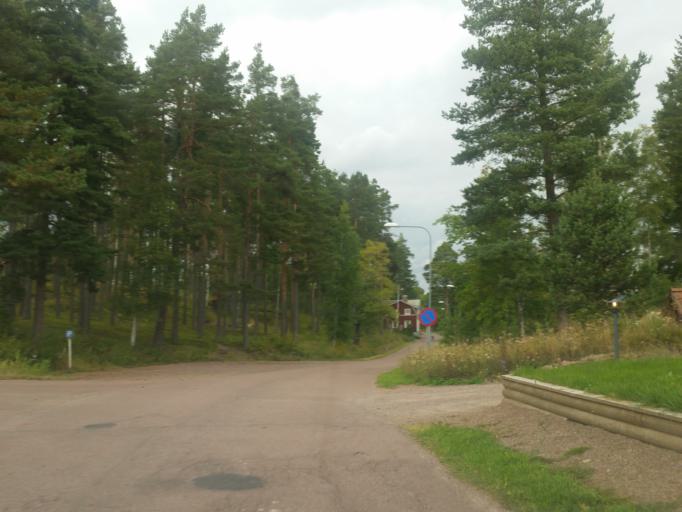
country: SE
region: Dalarna
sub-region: Leksand Municipality
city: Smedby
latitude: 60.6753
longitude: 15.1044
